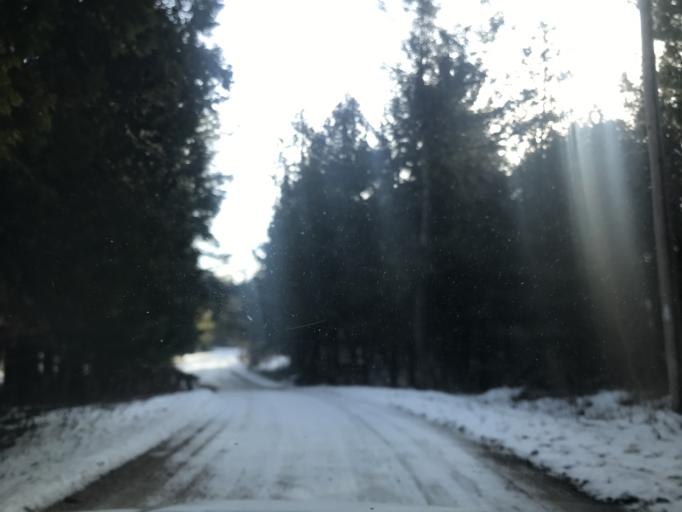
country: US
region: Wisconsin
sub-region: Door County
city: Sturgeon Bay
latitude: 45.1509
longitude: -87.0388
